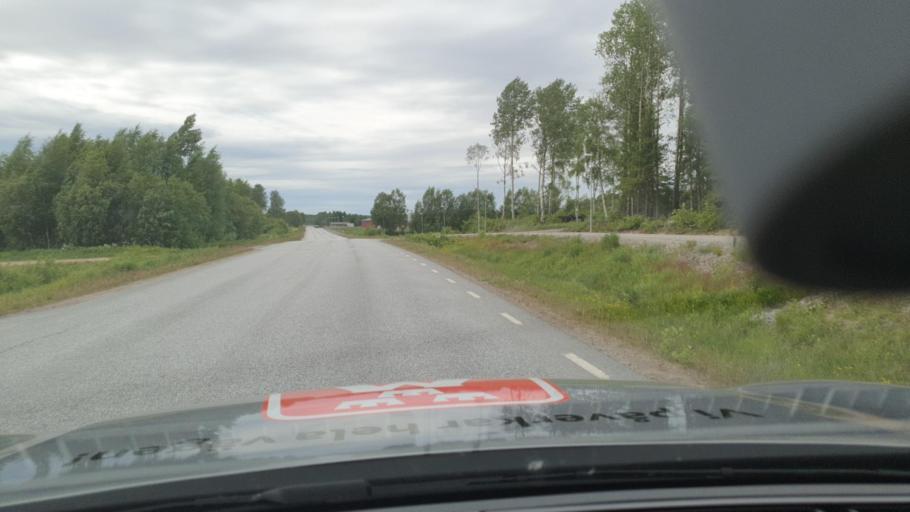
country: SE
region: Norrbotten
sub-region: Kalix Kommun
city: Rolfs
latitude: 65.8788
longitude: 23.0914
